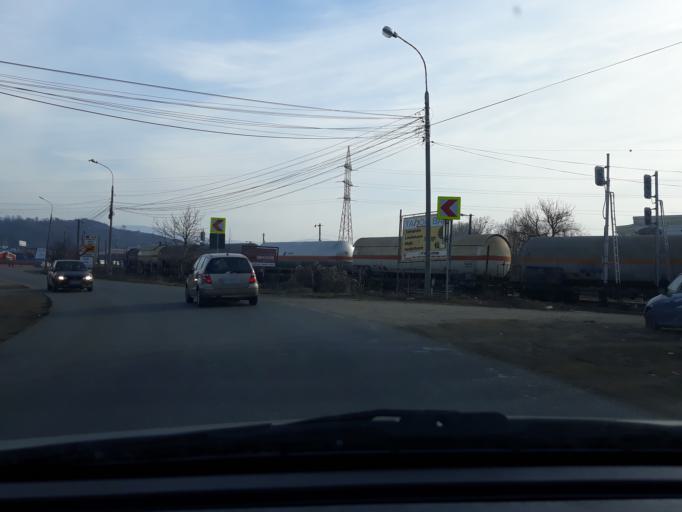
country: RO
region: Salaj
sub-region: Comuna Criseni
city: Criseni
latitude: 47.2235
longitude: 23.0396
